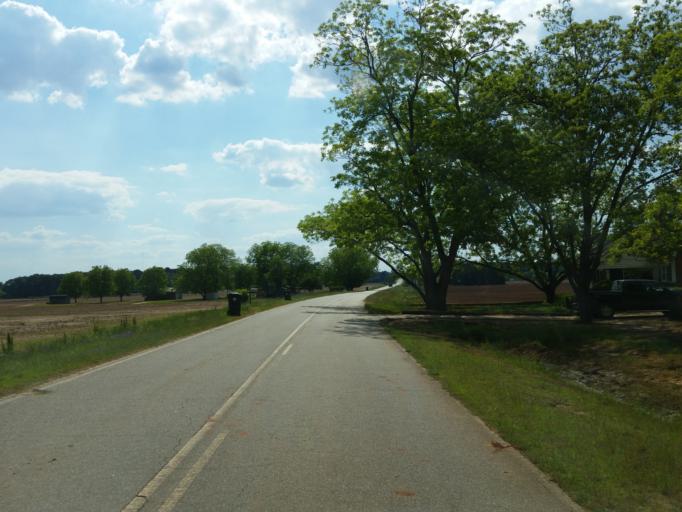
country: US
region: Georgia
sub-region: Houston County
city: Centerville
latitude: 32.5782
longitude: -83.7310
